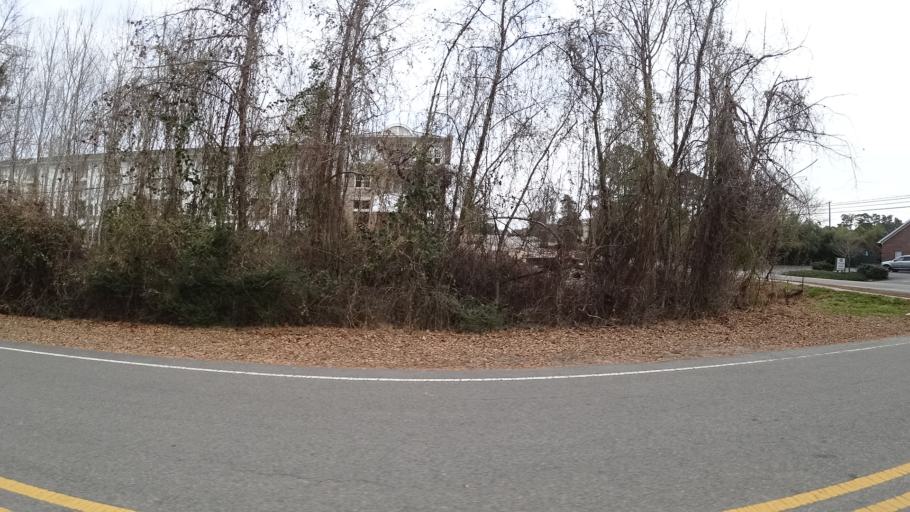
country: US
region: North Carolina
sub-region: Moore County
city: Pinehurst
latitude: 35.2008
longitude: -79.4706
